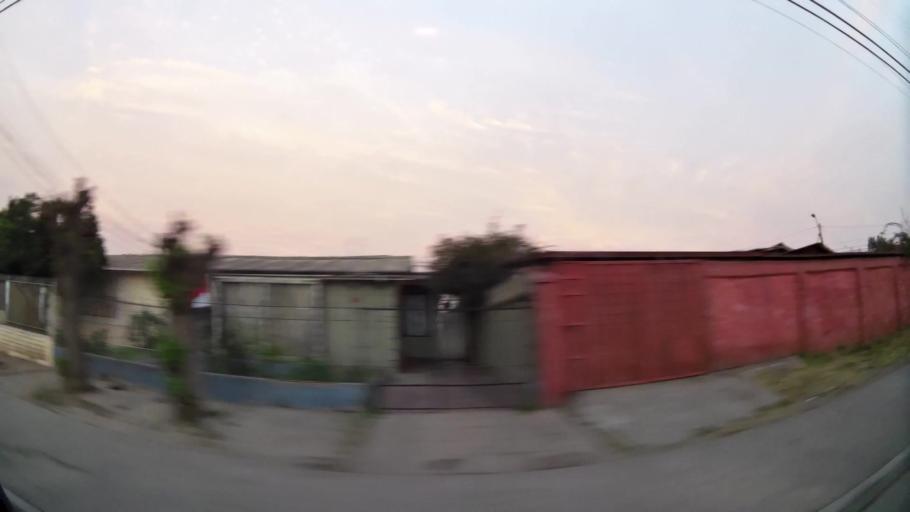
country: CL
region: Santiago Metropolitan
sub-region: Provincia de Santiago
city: Lo Prado
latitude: -33.5055
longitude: -70.7375
